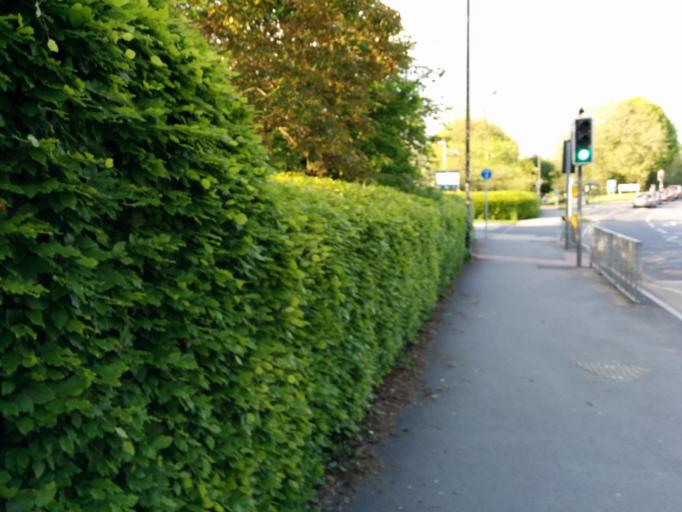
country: GB
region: England
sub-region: Hampshire
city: Alton
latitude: 51.1594
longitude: -0.9589
